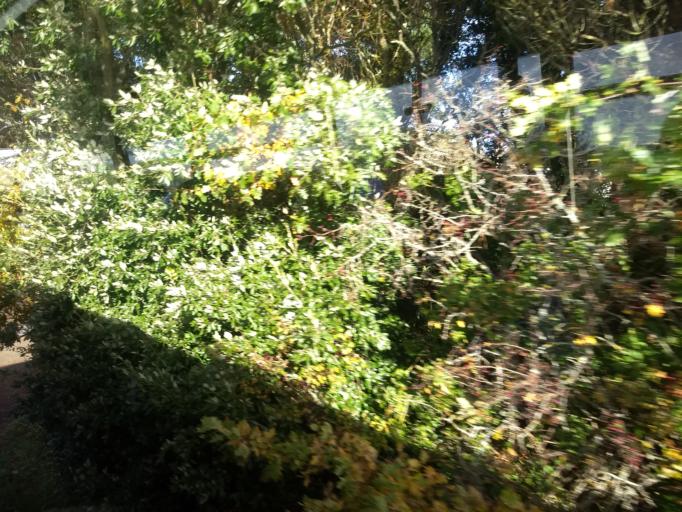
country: GB
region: England
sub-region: Isle of Wight
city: Yarmouth
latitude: 50.7049
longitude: -1.4857
